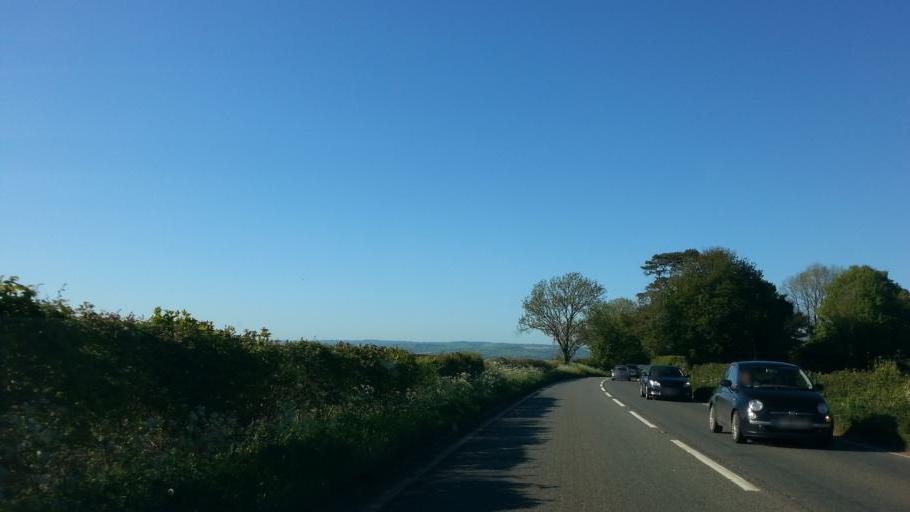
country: GB
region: England
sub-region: Somerset
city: Castle Cary
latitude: 51.0853
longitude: -2.5056
